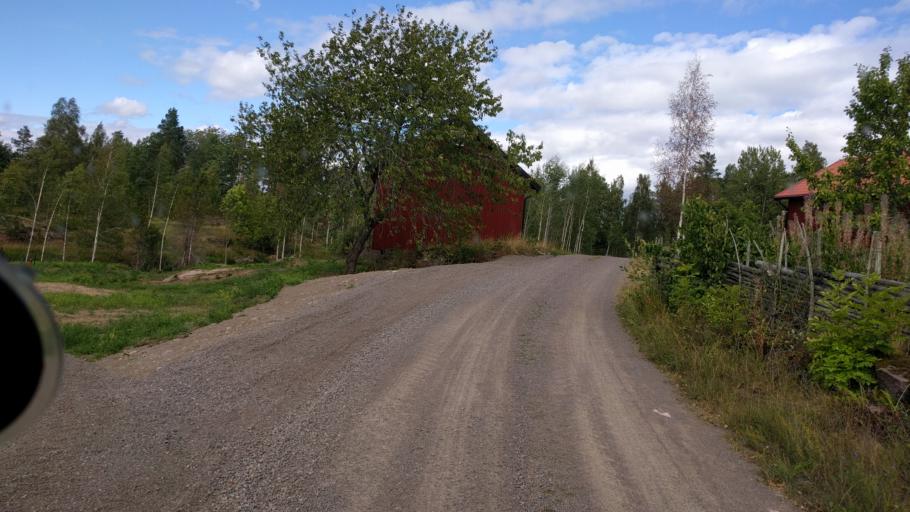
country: SE
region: Kalmar
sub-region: Vasterviks Kommun
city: Ankarsrum
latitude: 57.7265
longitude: 16.0931
